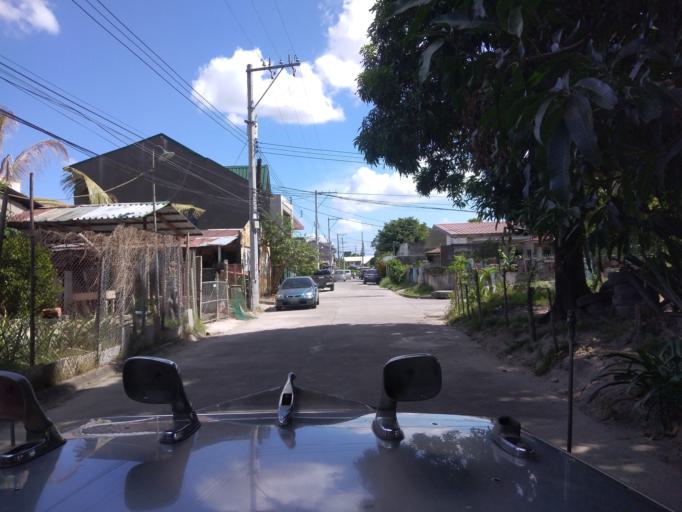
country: PH
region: Central Luzon
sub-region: Province of Pampanga
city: Calibutbut
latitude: 15.1144
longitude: 120.5976
